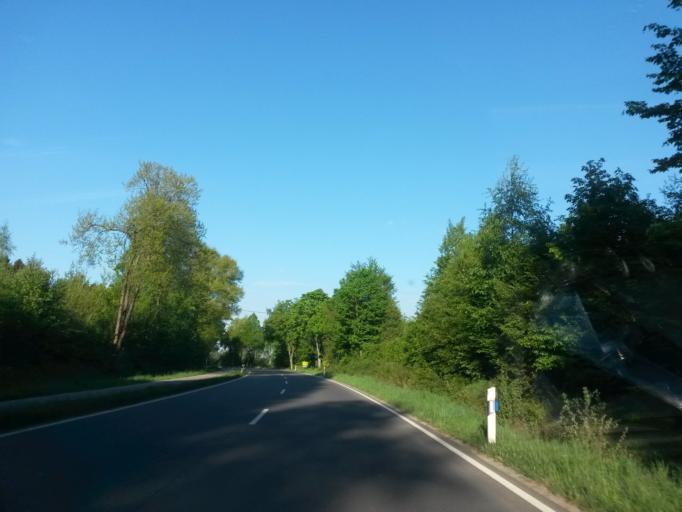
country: DE
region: North Rhine-Westphalia
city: Wiehl
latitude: 50.9287
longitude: 7.5039
